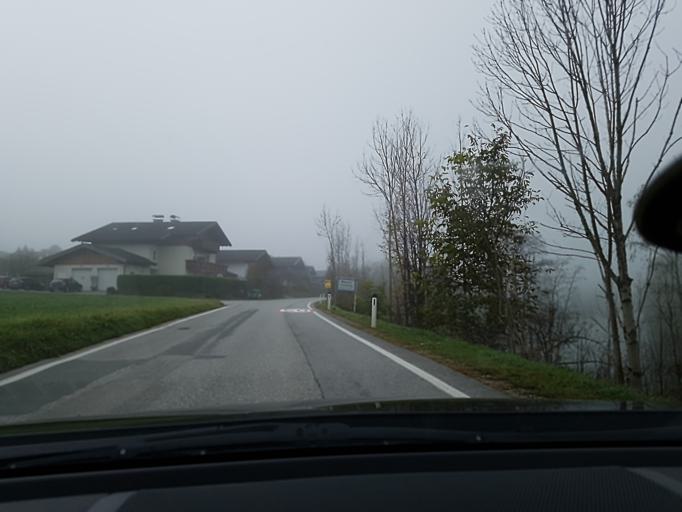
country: AT
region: Salzburg
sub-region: Politischer Bezirk Sankt Johann im Pongau
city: Sankt Johann im Pongau
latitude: 47.3788
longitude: 13.2154
